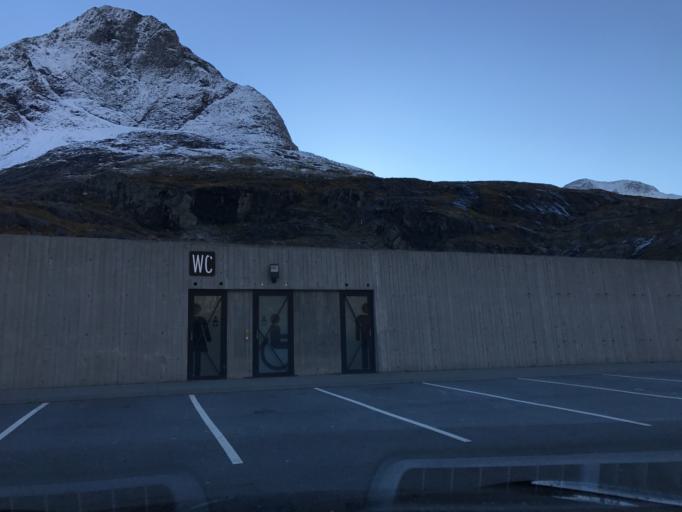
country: NO
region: More og Romsdal
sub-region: Rauma
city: Andalsnes
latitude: 62.4535
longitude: 7.6639
